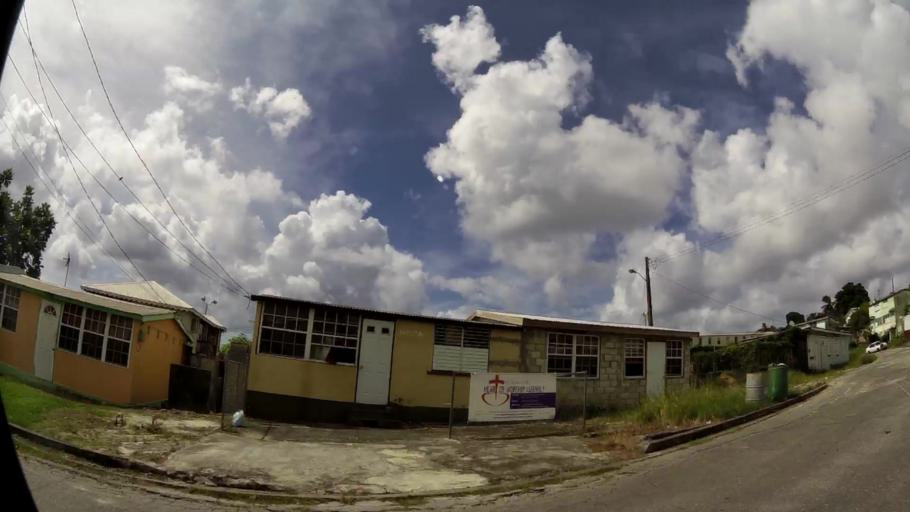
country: BB
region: Saint Michael
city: Bridgetown
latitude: 13.1302
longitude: -59.6169
